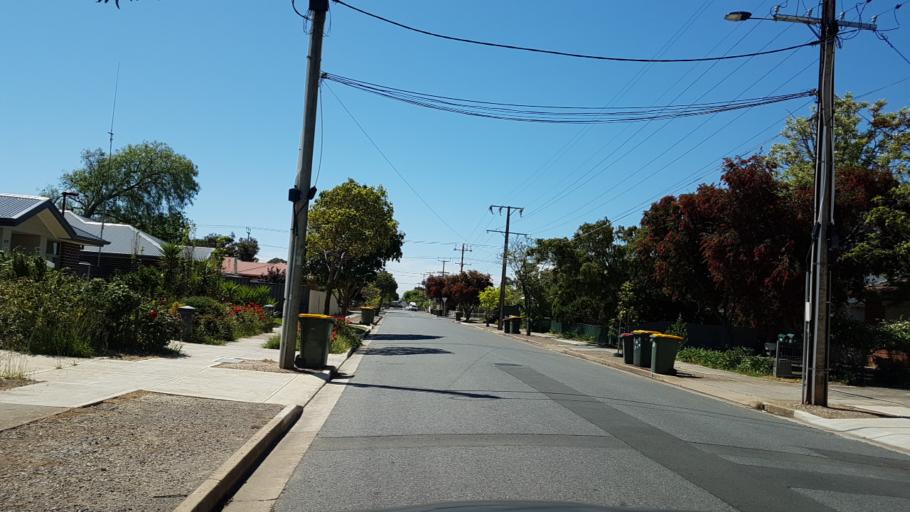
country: AU
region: South Australia
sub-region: Marion
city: South Plympton
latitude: -34.9783
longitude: 138.5515
